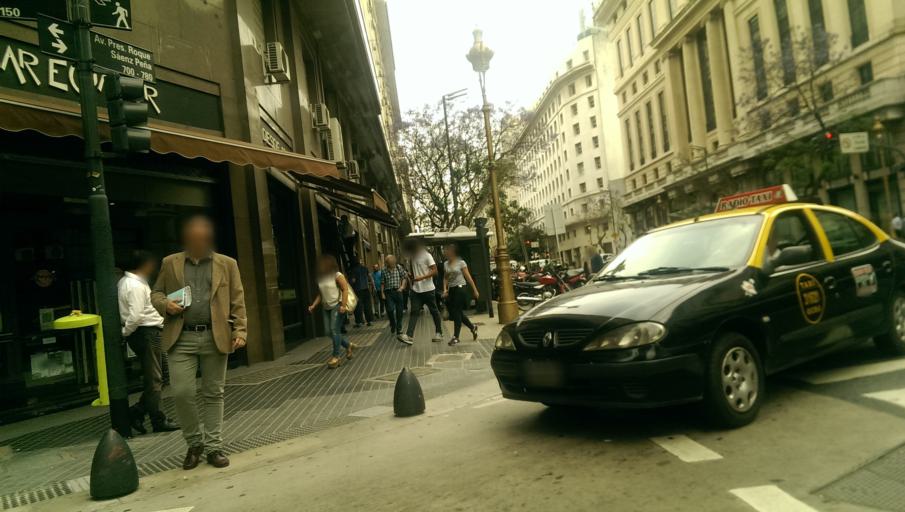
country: AR
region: Buenos Aires F.D.
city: Buenos Aires
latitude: -34.6063
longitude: -58.3764
